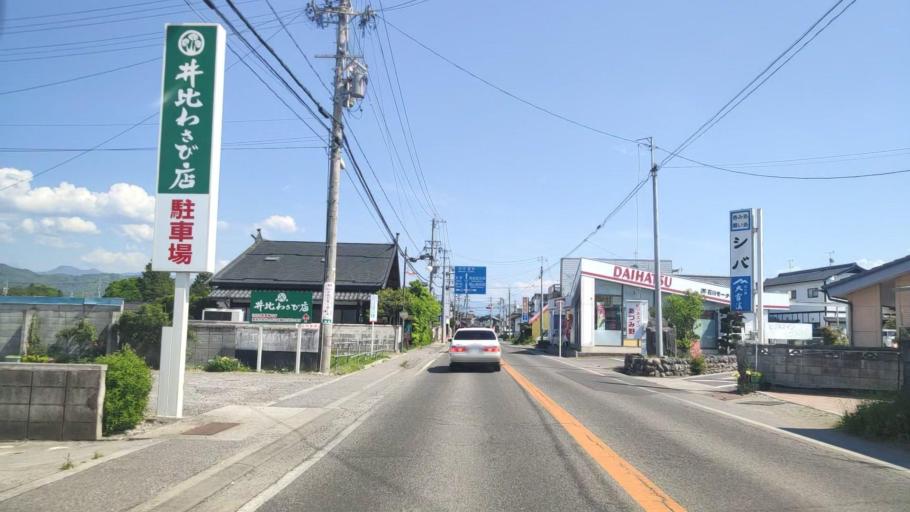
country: JP
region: Nagano
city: Hotaka
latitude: 36.3464
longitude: 137.8850
